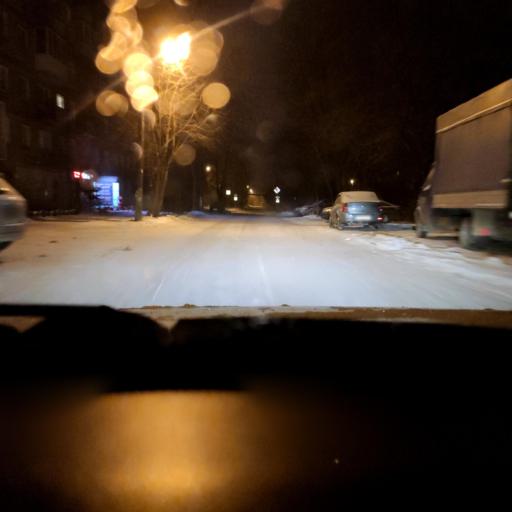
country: RU
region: Perm
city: Polazna
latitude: 58.1358
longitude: 56.3804
